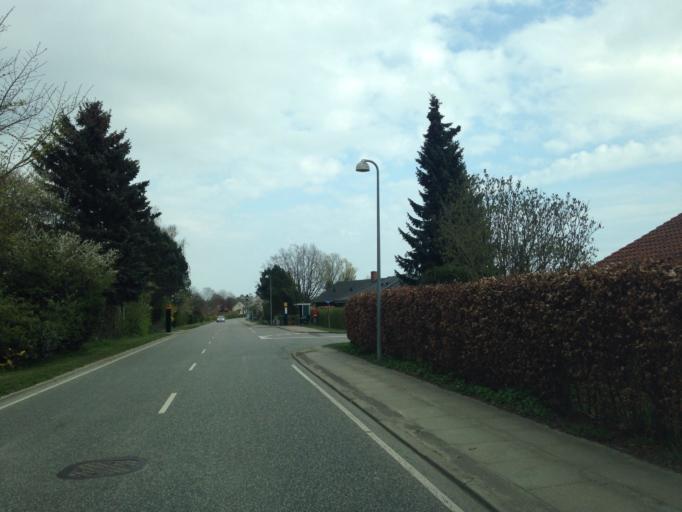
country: DK
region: Capital Region
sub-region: Hoje-Taastrup Kommune
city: Taastrup
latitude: 55.6295
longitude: 12.2865
